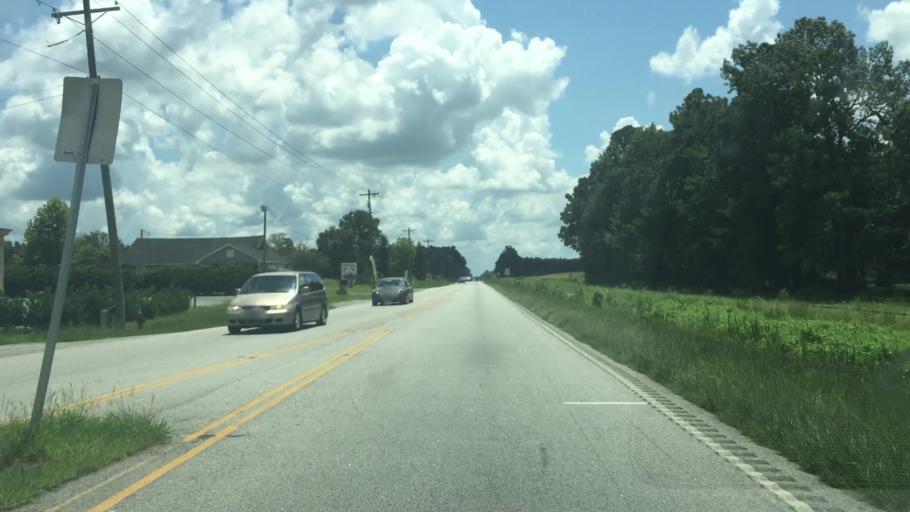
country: US
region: North Carolina
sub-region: Columbus County
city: Tabor City
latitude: 34.1316
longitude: -78.8761
